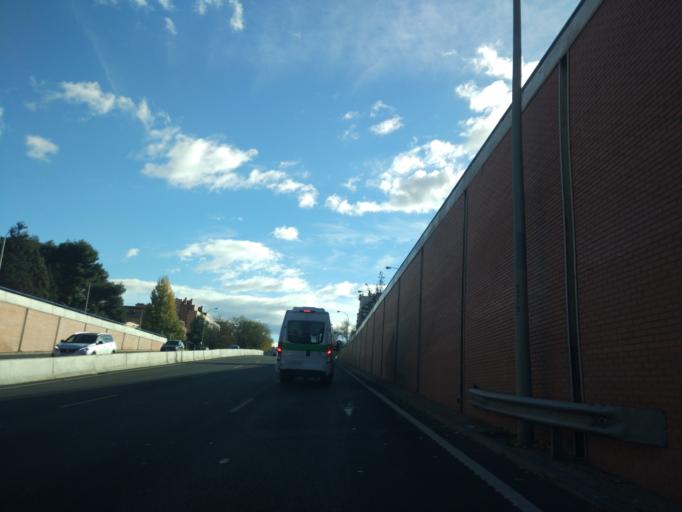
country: ES
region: Madrid
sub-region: Provincia de Madrid
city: Usera
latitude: 40.3747
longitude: -3.6950
